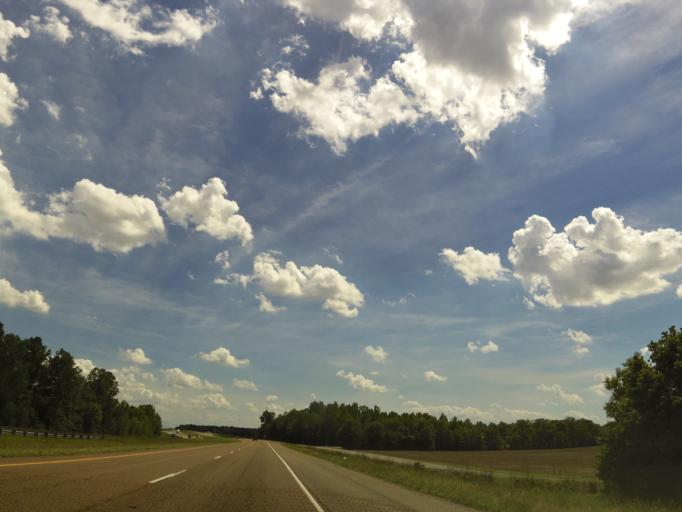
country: US
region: Tennessee
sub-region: Dyer County
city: Dyersburg
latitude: 36.0351
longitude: -89.3394
